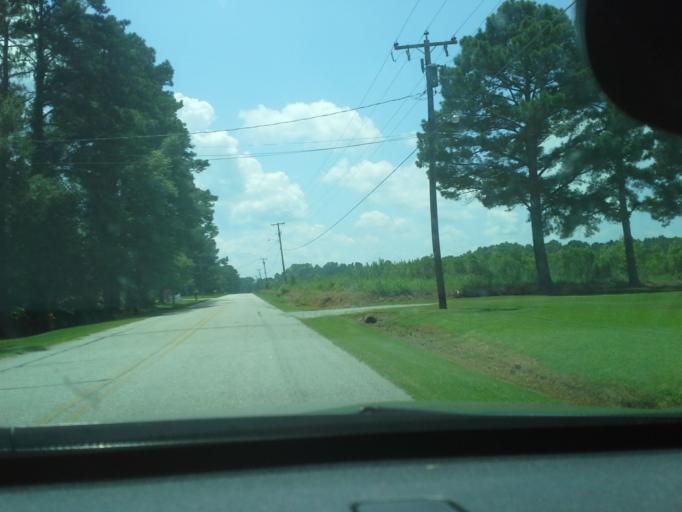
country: US
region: North Carolina
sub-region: Washington County
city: Plymouth
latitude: 35.8451
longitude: -76.7616
